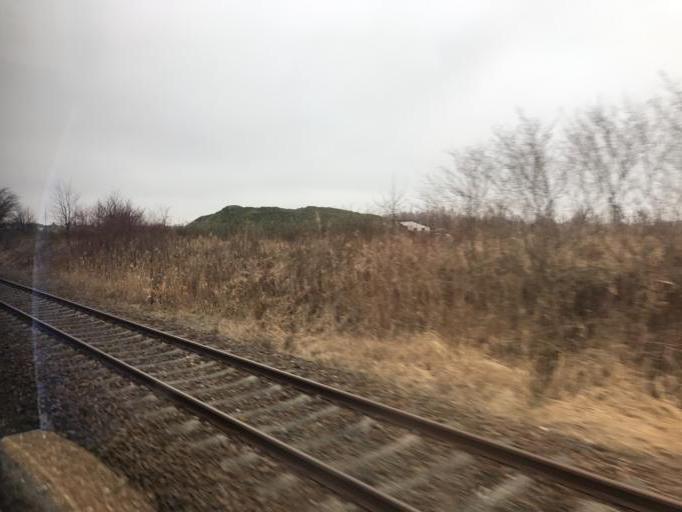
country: DE
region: Mecklenburg-Vorpommern
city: Pasewalk
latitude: 53.5094
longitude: 14.0187
